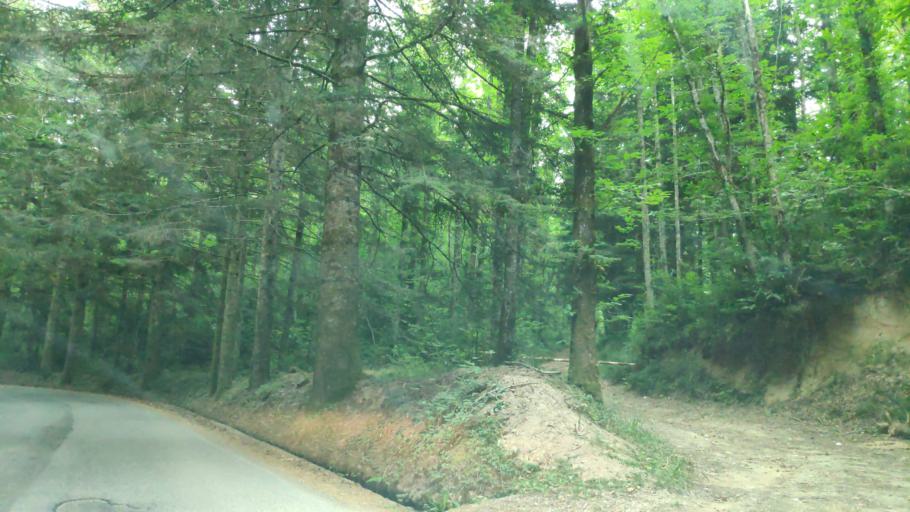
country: IT
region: Calabria
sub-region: Provincia di Vibo-Valentia
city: Mongiana
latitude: 38.5143
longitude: 16.3093
